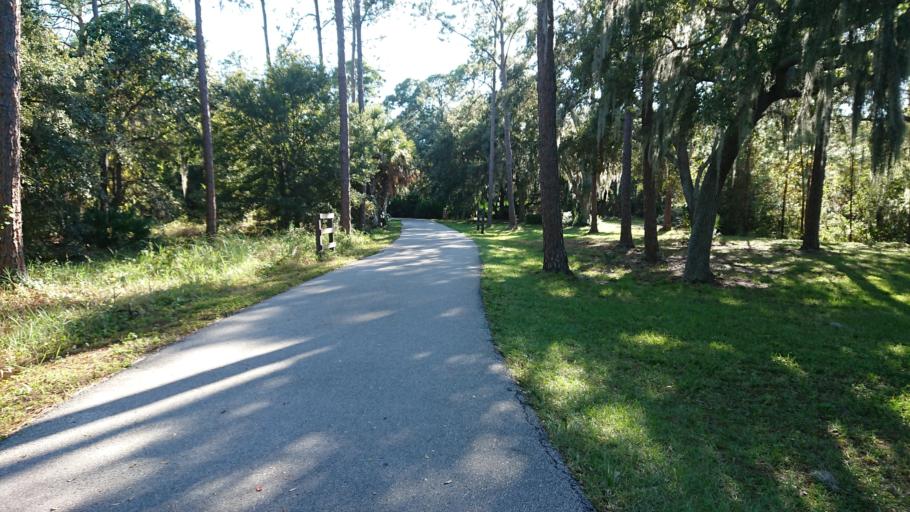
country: US
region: Florida
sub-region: Pinellas County
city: Seminole
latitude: 27.8487
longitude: -82.7750
